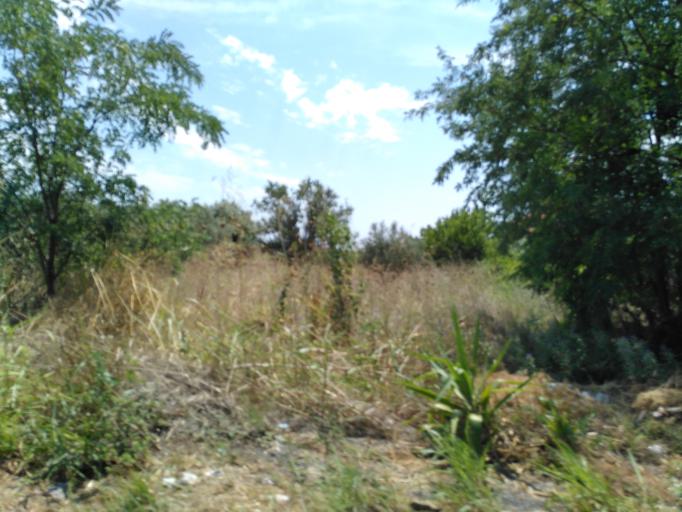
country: GR
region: Central Macedonia
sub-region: Nomos Thessalonikis
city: Epanomi
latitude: 40.4316
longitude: 22.9053
